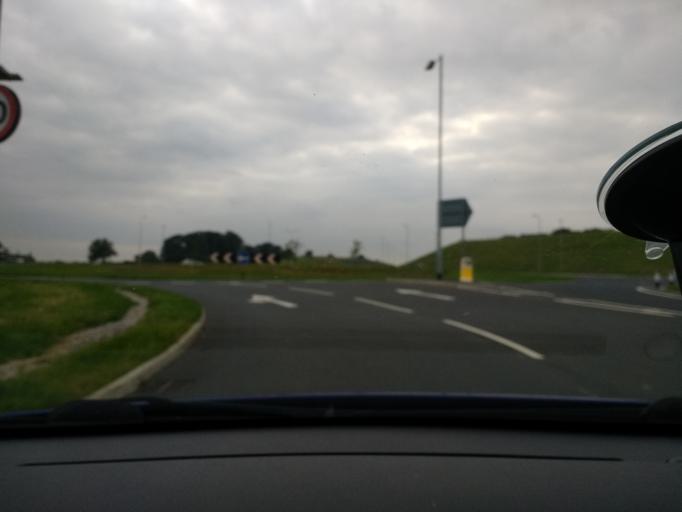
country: GB
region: England
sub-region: Lancashire
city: Bolton le Sands
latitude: 54.0771
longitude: -2.7731
